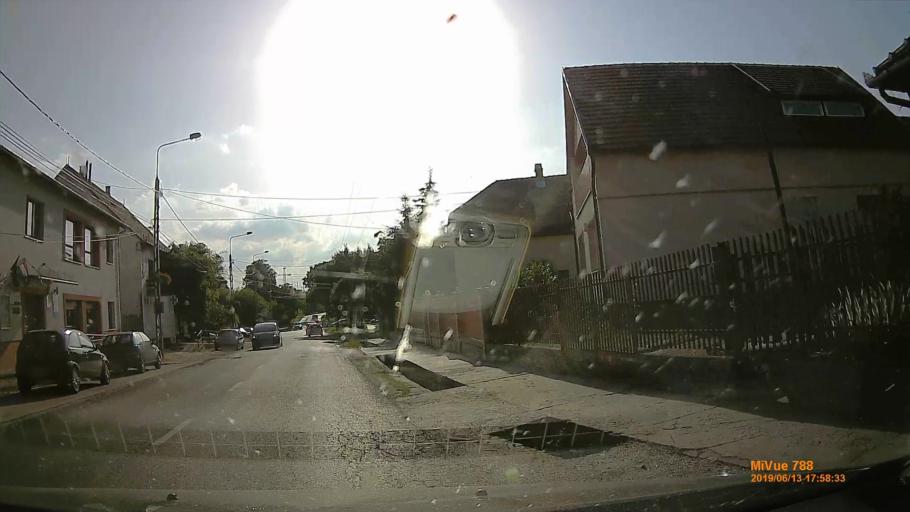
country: HU
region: Pest
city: Ecser
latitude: 47.4445
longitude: 19.3216
